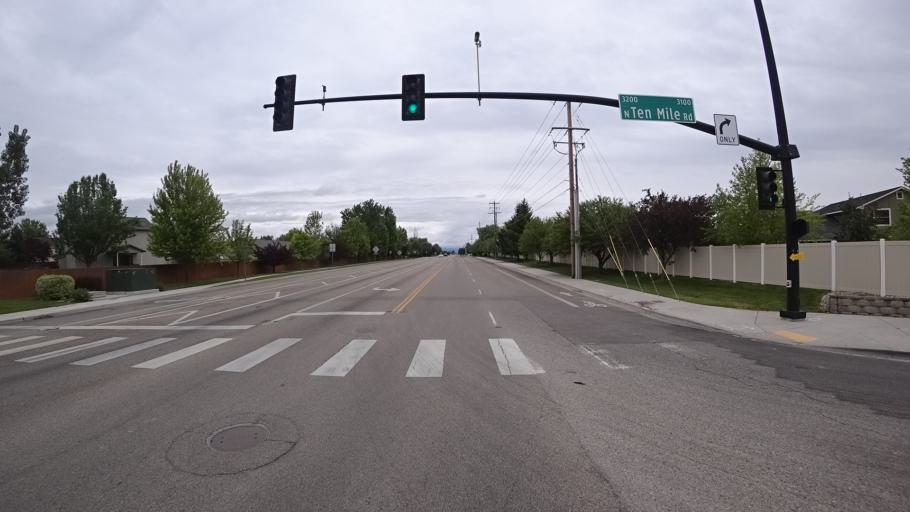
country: US
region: Idaho
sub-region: Ada County
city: Meridian
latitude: 43.6340
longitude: -116.4335
